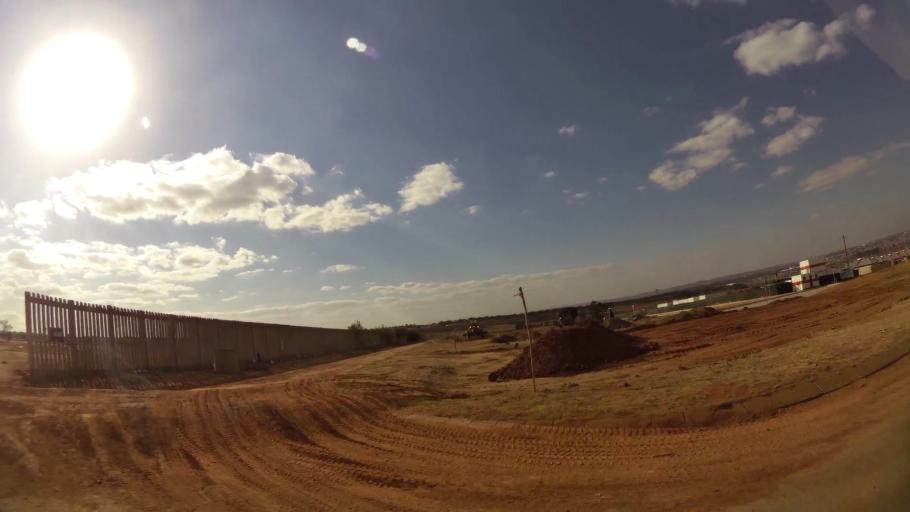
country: ZA
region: Gauteng
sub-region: Ekurhuleni Metropolitan Municipality
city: Tembisa
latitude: -25.9800
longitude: 28.1847
